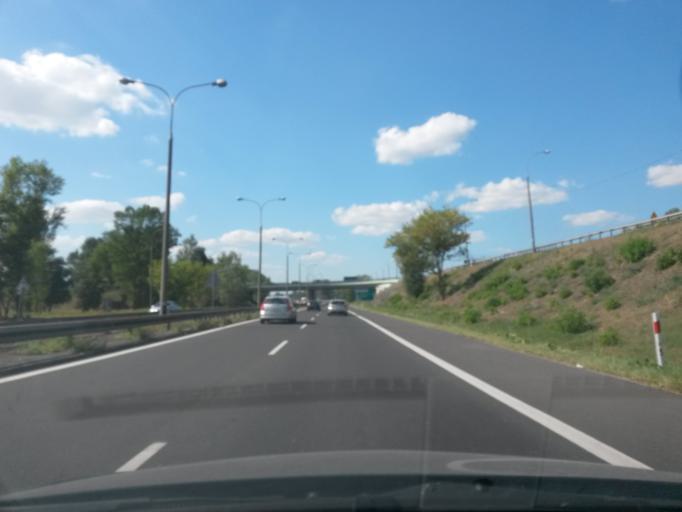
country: PL
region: Masovian Voivodeship
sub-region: Powiat nowodworski
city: Nowy Dwor Mazowiecki
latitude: 52.4096
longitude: 20.6993
